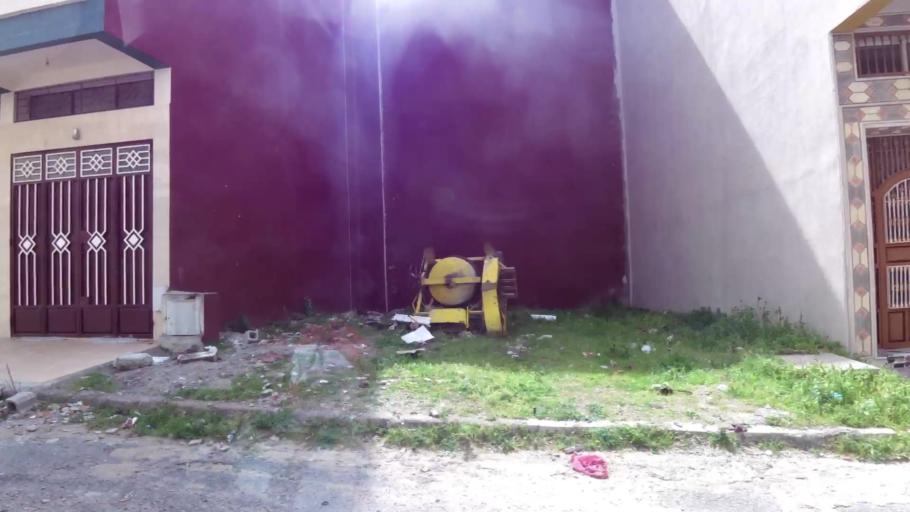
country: MA
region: Tanger-Tetouan
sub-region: Tanger-Assilah
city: Tangier
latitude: 35.7434
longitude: -5.8369
